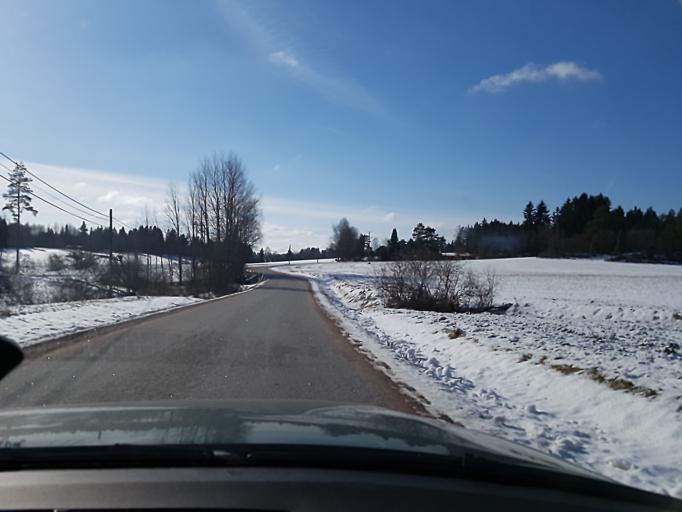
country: FI
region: Uusimaa
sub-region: Raaseporin
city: Inga
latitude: 60.0836
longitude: 24.0734
